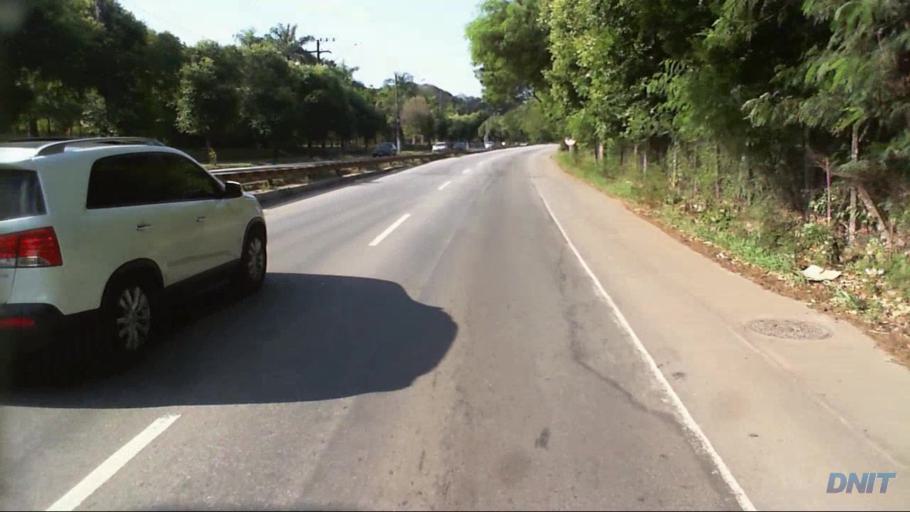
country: BR
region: Minas Gerais
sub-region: Ipatinga
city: Ipatinga
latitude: -19.4896
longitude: -42.5610
